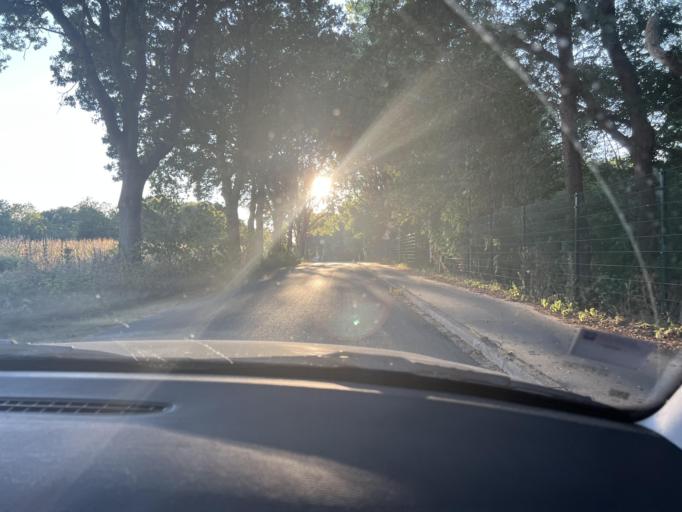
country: DE
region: Schleswig-Holstein
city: Weddingstedt
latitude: 54.2203
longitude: 9.0932
